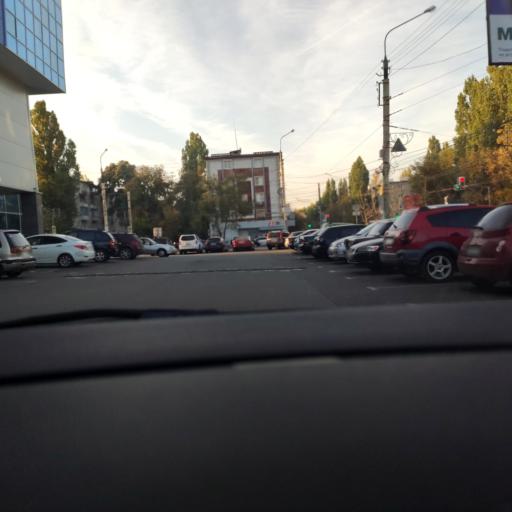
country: RU
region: Voronezj
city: Voronezh
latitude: 51.6532
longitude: 39.1491
